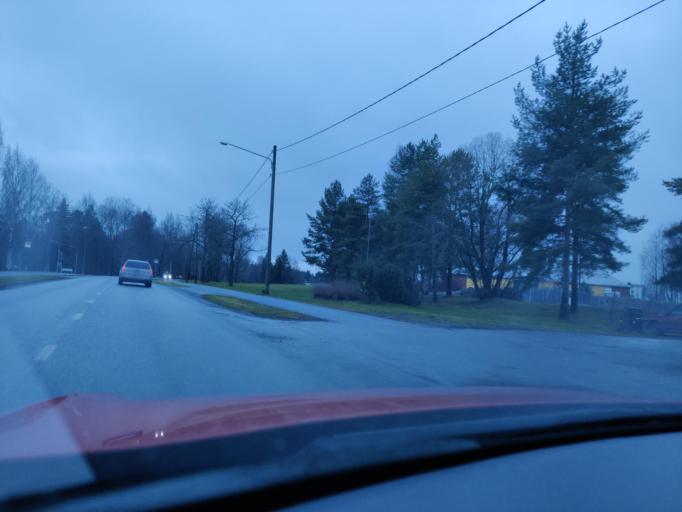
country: FI
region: Pirkanmaa
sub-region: Tampere
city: Nokia
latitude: 61.4842
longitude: 23.5300
